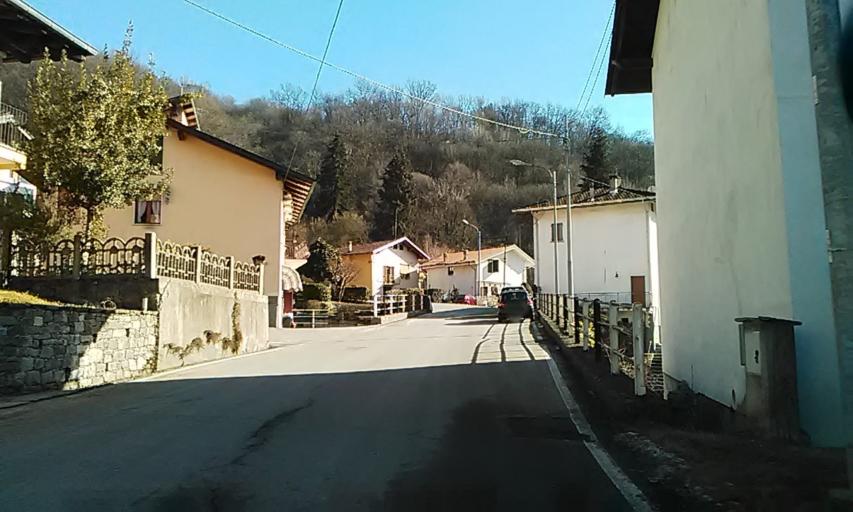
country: IT
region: Piedmont
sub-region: Provincia di Vercelli
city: Cellio
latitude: 45.7342
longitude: 8.3008
